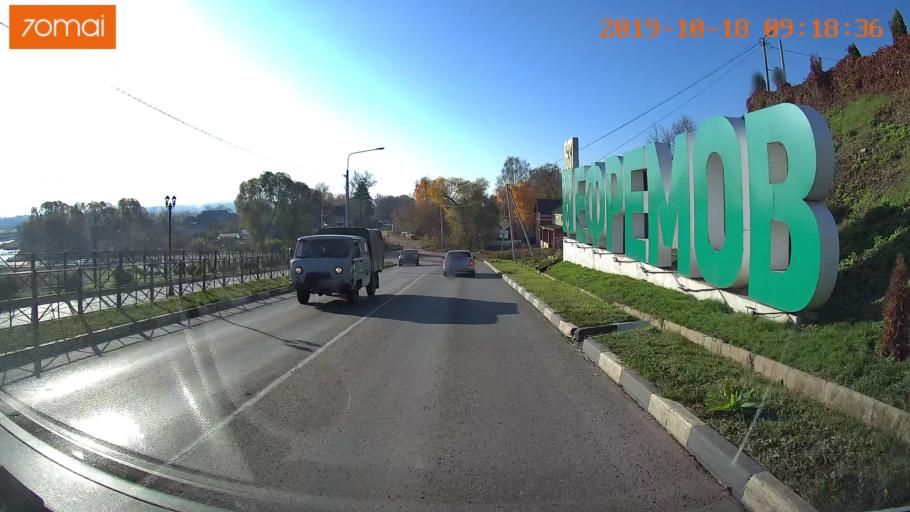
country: RU
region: Tula
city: Yefremov
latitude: 53.1357
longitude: 38.1206
